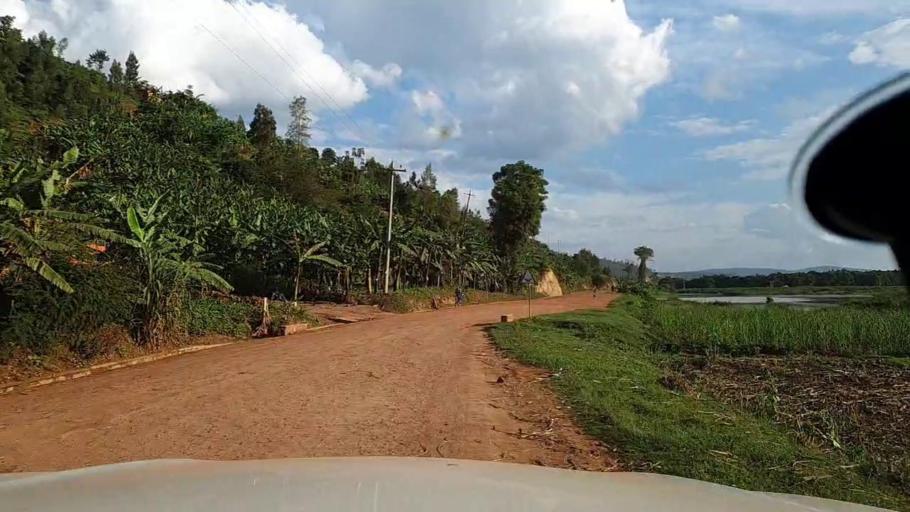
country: RW
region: Kigali
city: Kigali
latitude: -1.9339
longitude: 29.9971
